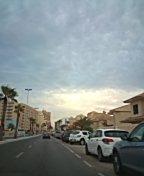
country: ES
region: Murcia
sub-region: Murcia
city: La Manga del Mar Menor
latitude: 37.7013
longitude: -0.7407
